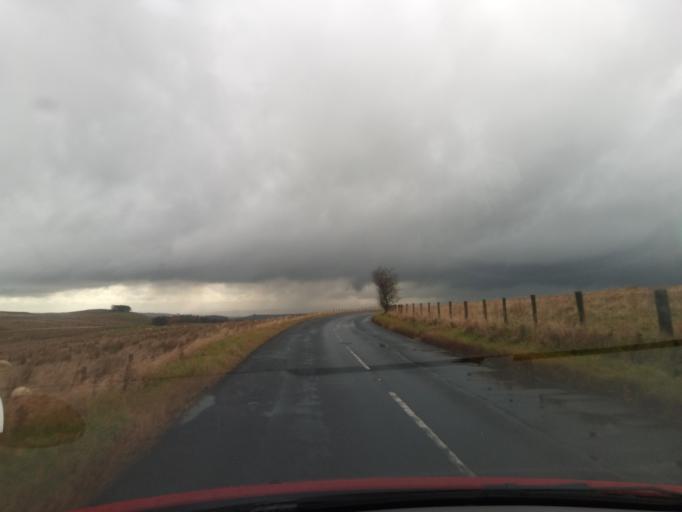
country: GB
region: England
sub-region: Northumberland
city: Corsenside
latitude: 55.1729
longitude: -2.2583
